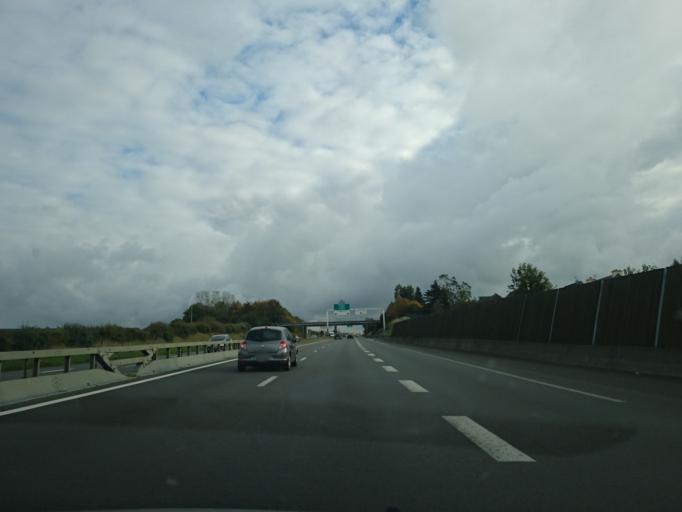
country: FR
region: Brittany
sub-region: Departement des Cotes-d'Armor
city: Langueux
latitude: 48.5027
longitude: -2.7302
